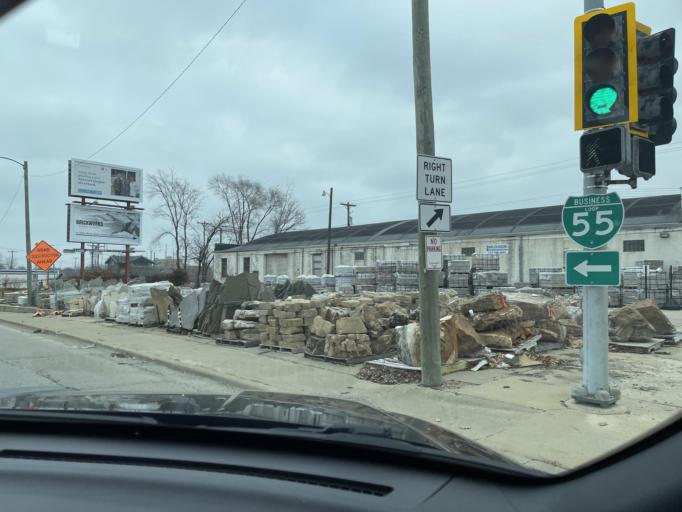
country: US
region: Illinois
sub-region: Sangamon County
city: Springfield
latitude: 39.7938
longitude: -89.6437
